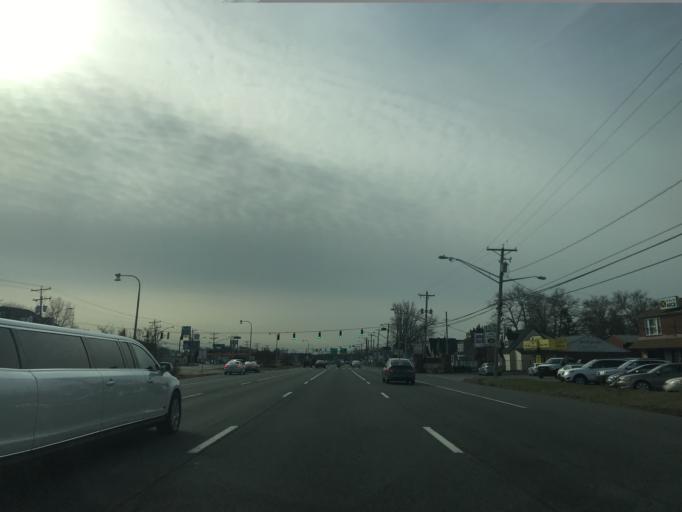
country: US
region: Delaware
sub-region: New Castle County
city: Wilmington Manor
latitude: 39.6593
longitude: -75.6113
